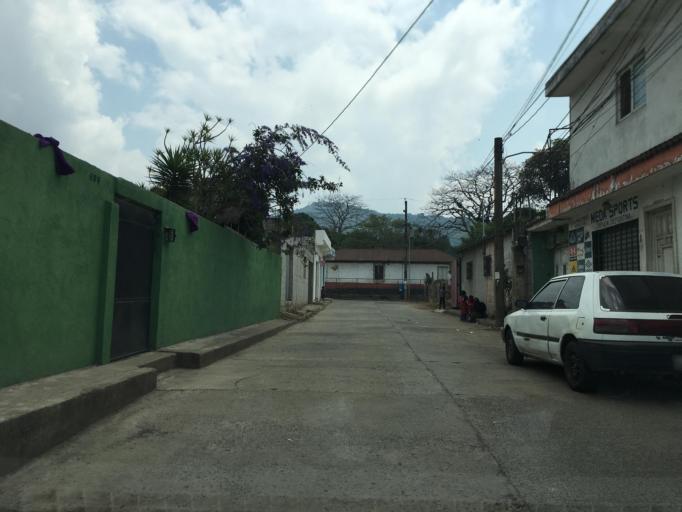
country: GT
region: Guatemala
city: Villa Canales
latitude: 14.4043
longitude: -90.5431
